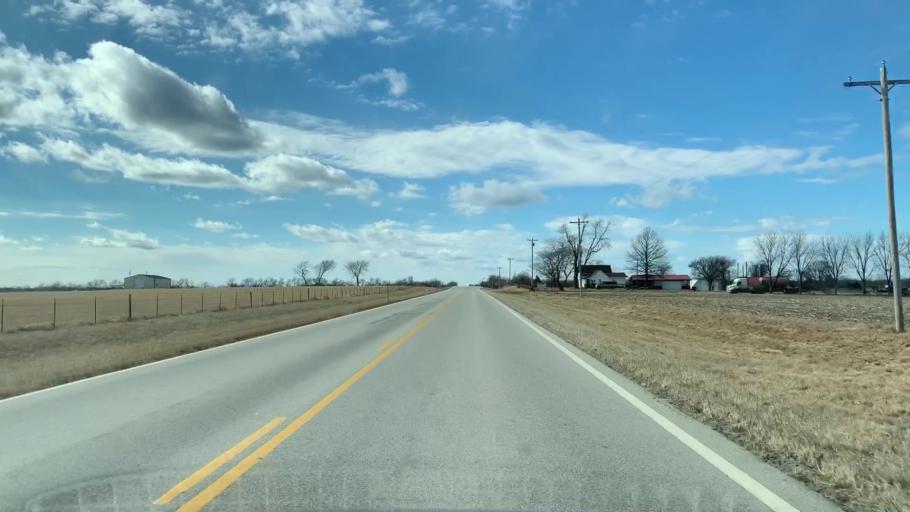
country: US
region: Kansas
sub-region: Neosho County
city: Chanute
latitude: 37.5290
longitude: -95.4118
